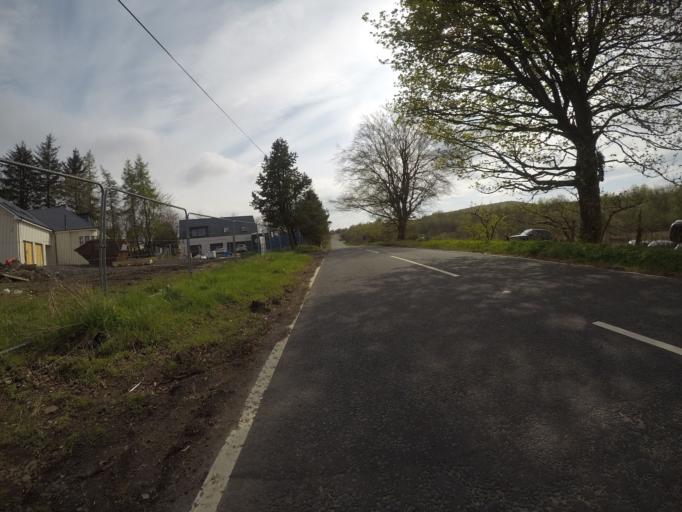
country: GB
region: Scotland
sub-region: East Renfrewshire
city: Newton Mearns
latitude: 55.7456
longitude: -4.3619
